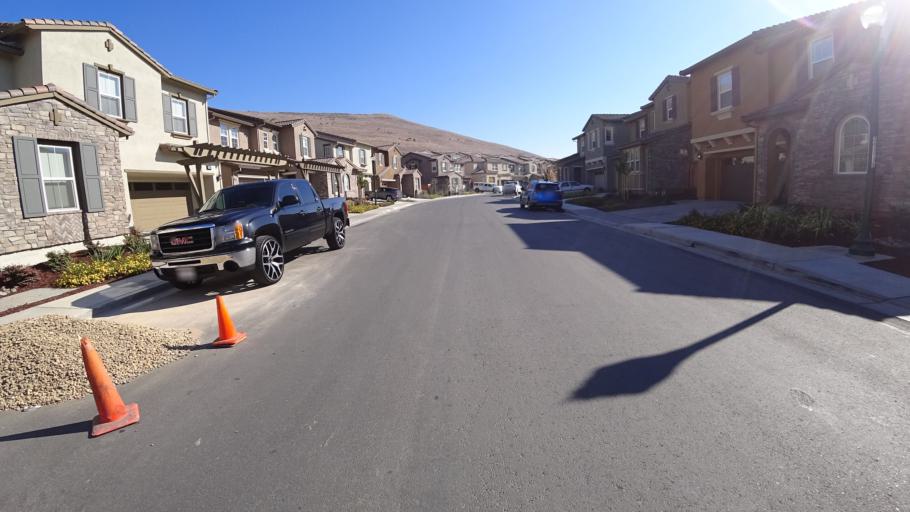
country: US
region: California
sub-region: Alameda County
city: Fairview
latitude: 37.6395
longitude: -122.0481
